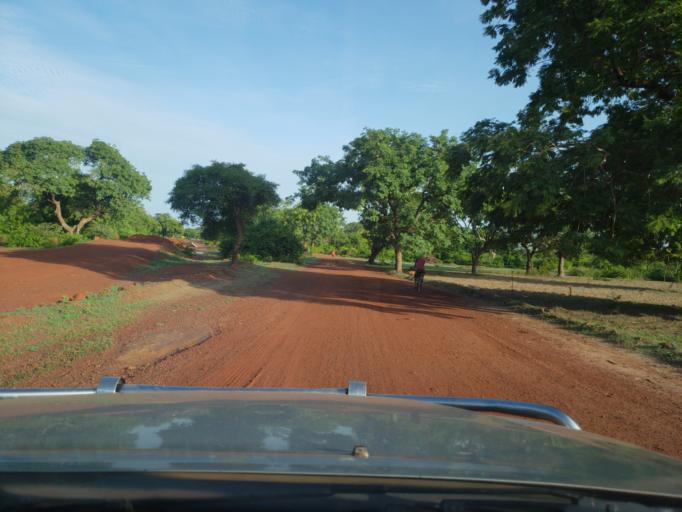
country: ML
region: Sikasso
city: Koutiala
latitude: 12.4221
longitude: -5.5863
